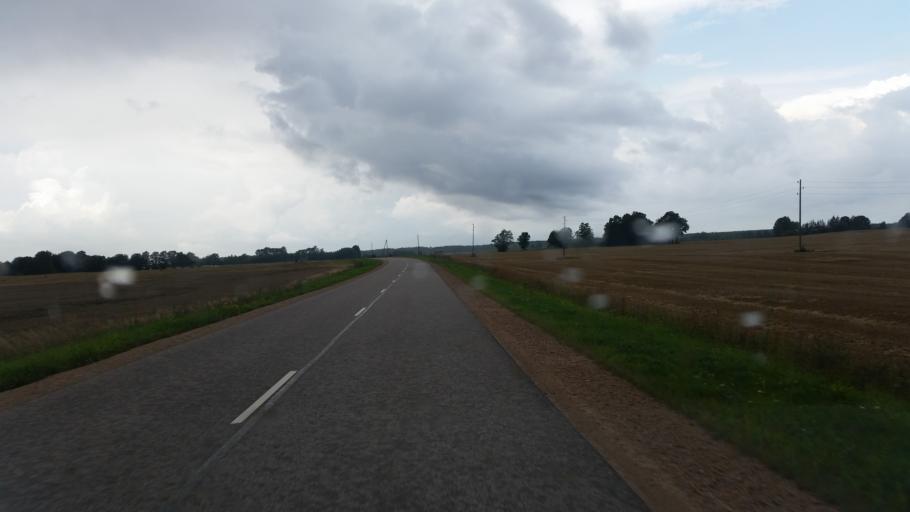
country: LV
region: Vecumnieki
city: Vecumnieki
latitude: 56.4331
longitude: 24.4315
